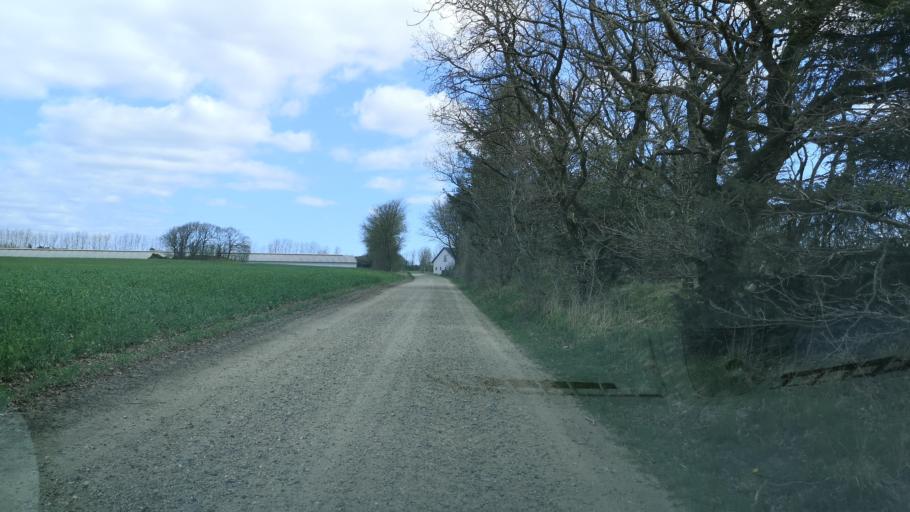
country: DK
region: Central Jutland
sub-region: Ringkobing-Skjern Kommune
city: Skjern
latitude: 55.9711
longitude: 8.5011
